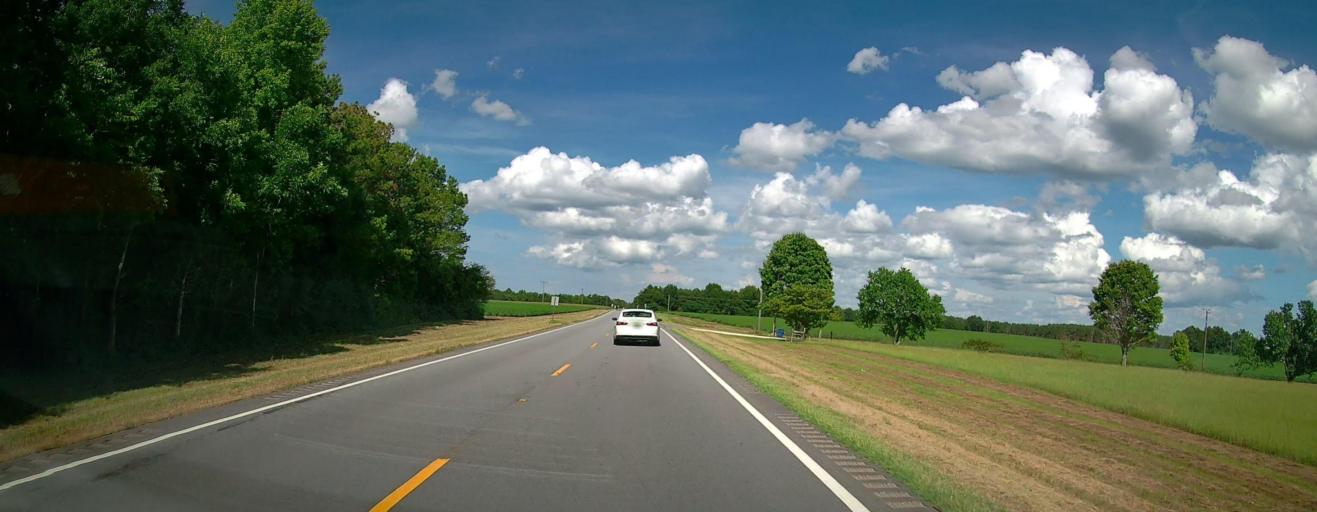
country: US
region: Alabama
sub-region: Lee County
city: Auburn
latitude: 32.4306
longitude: -85.4306
